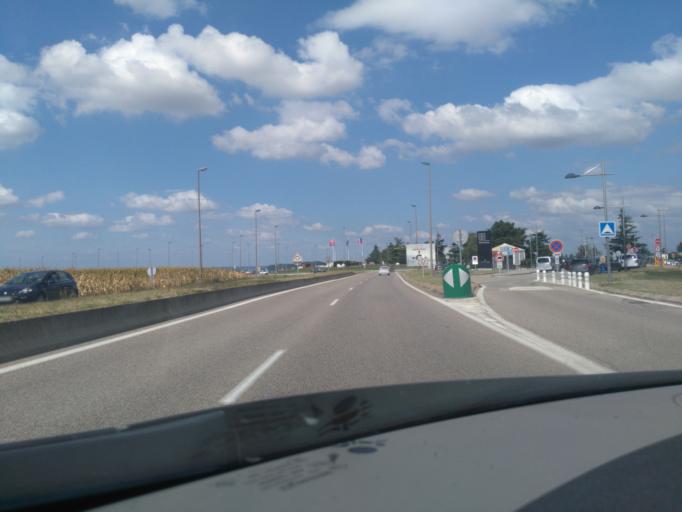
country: FR
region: Rhone-Alpes
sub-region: Departement du Rhone
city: Saint-Laurent-de-Mure
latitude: 45.7153
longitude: 5.0706
